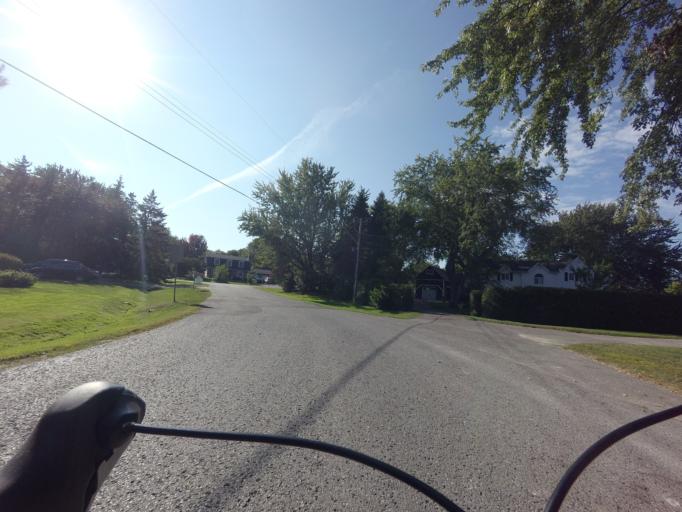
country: CA
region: Ontario
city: Bells Corners
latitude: 45.2339
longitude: -75.6846
